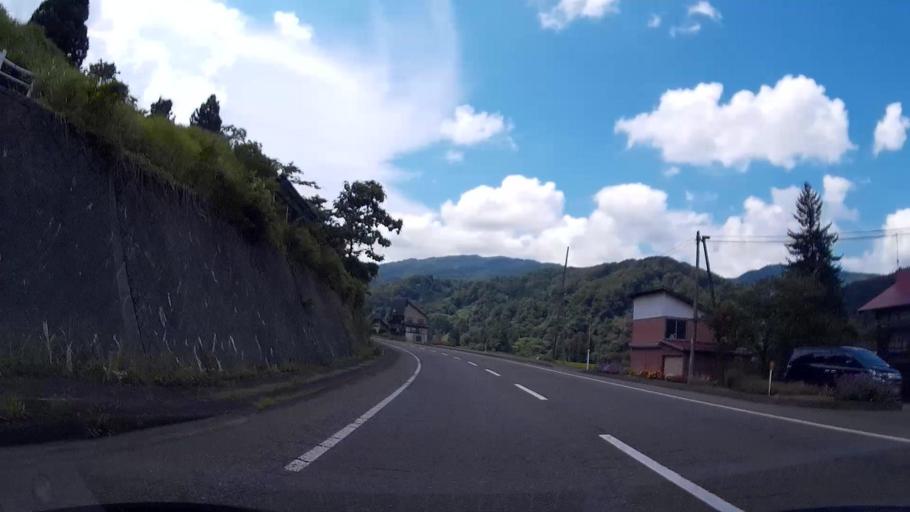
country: JP
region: Niigata
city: Tokamachi
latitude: 36.9949
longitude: 138.6034
